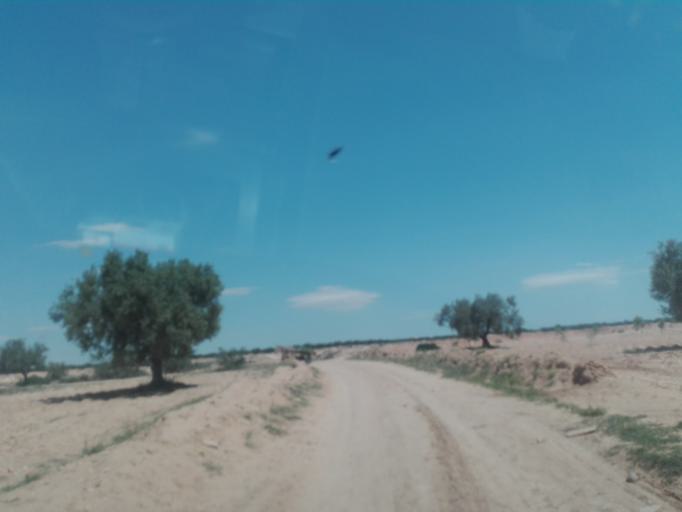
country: TN
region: Safaqis
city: Sfax
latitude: 34.6759
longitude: 10.6108
